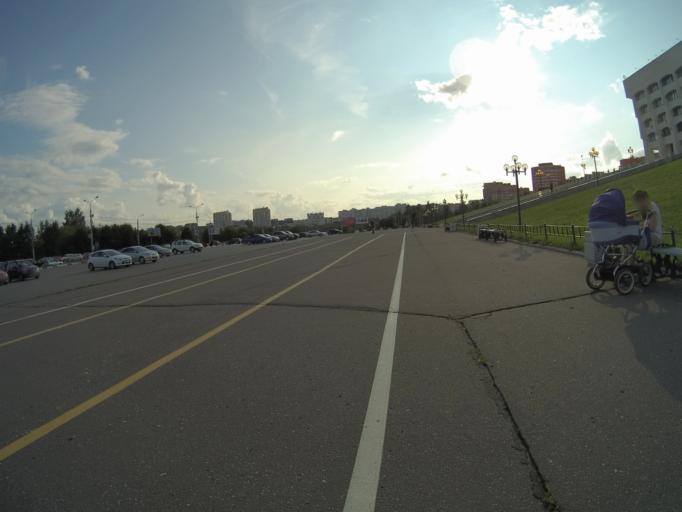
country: RU
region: Vladimir
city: Vladimir
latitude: 56.1368
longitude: 40.3899
